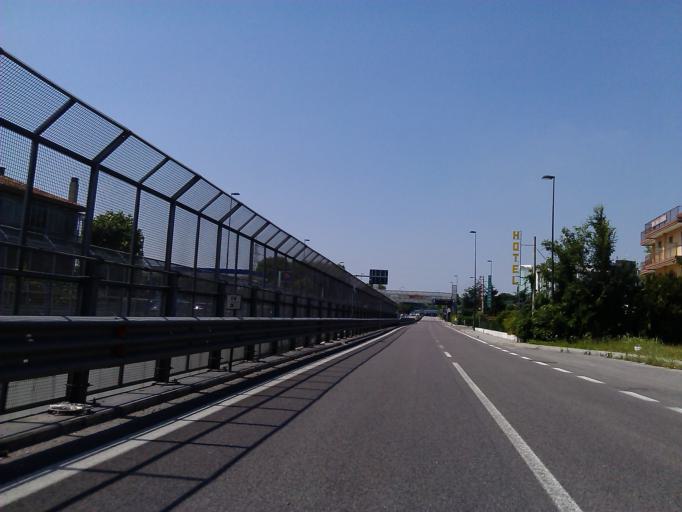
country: IT
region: Veneto
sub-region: Provincia di Venezia
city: Campalto
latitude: 45.4814
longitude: 12.2726
